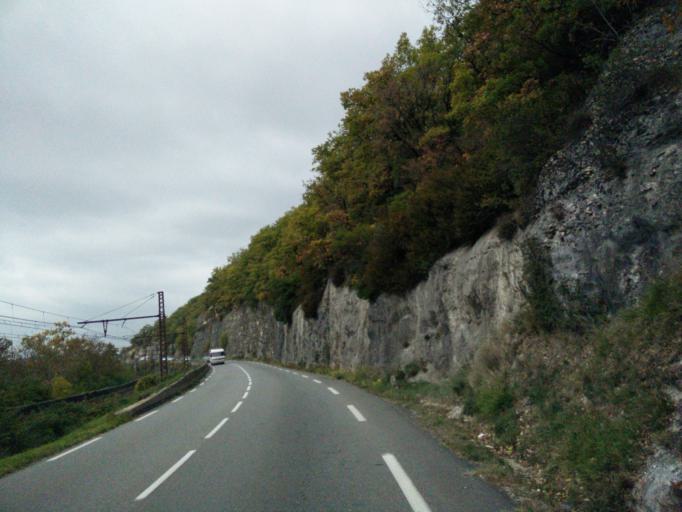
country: FR
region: Midi-Pyrenees
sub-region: Departement du Lot
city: Pradines
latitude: 44.4774
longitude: 1.4254
